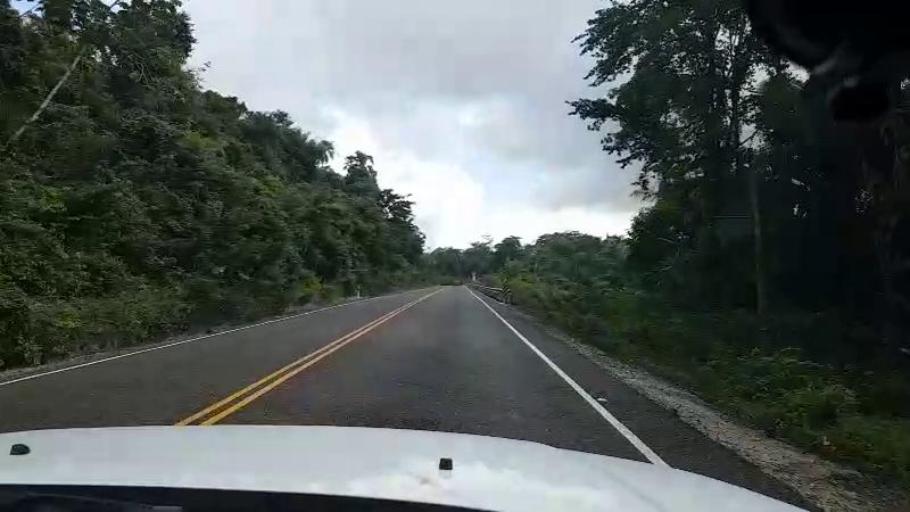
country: BZ
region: Cayo
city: Belmopan
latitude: 17.1549
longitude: -88.6797
